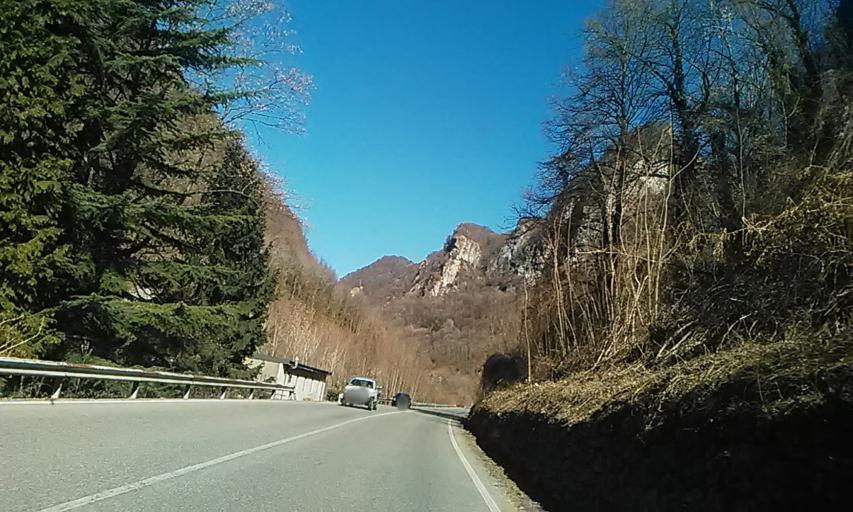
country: IT
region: Piedmont
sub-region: Provincia di Vercelli
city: Varallo
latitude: 45.7984
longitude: 8.2721
